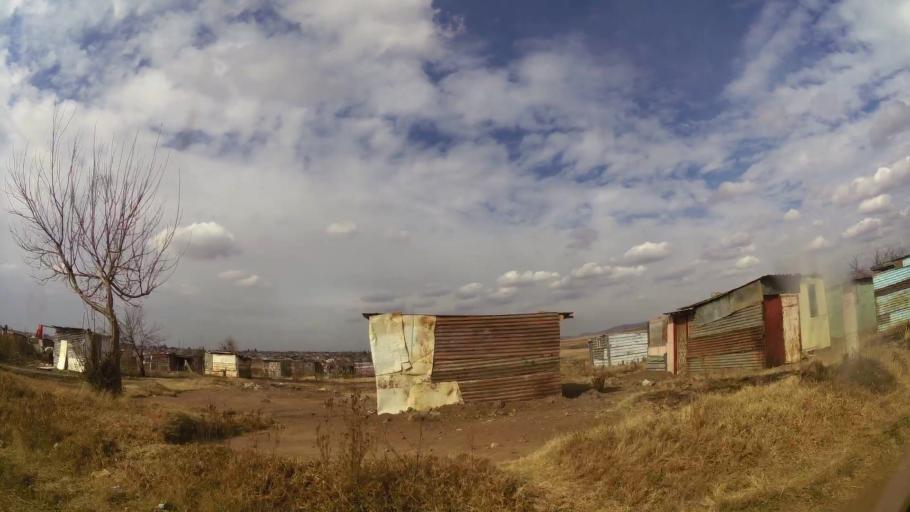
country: ZA
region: Gauteng
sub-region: Ekurhuleni Metropolitan Municipality
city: Germiston
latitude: -26.4192
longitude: 28.1644
